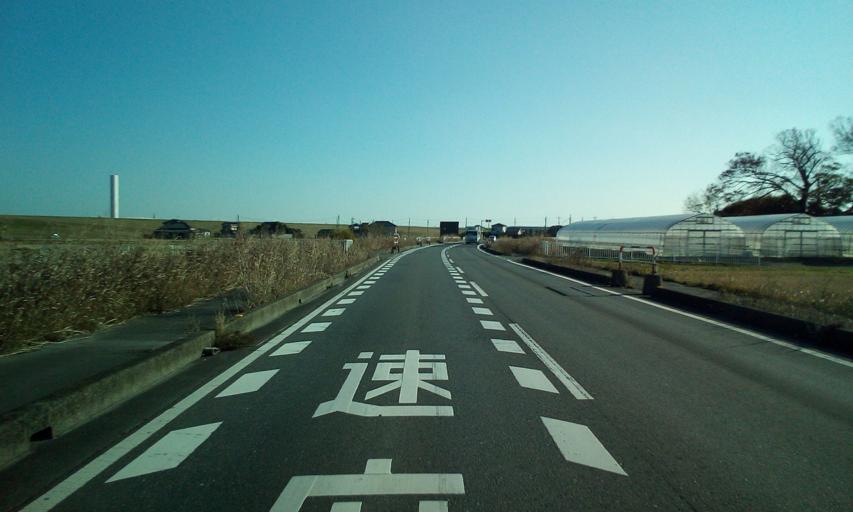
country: JP
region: Chiba
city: Nagareyama
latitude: 35.8853
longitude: 139.8857
